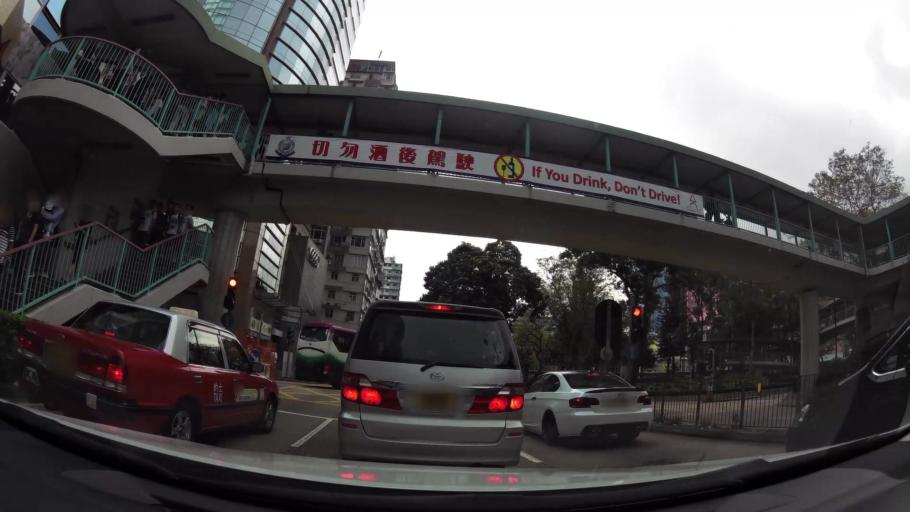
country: HK
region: Kowloon City
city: Kowloon
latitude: 22.3004
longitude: 114.1760
